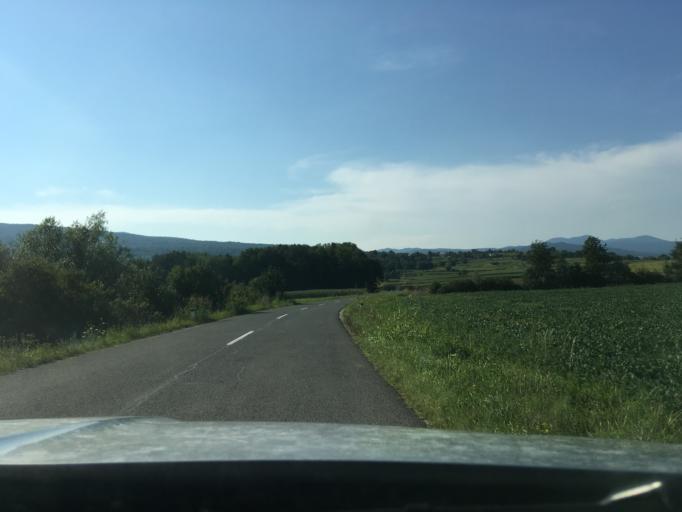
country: SI
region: Crnomelj
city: Crnomelj
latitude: 45.5231
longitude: 15.1667
